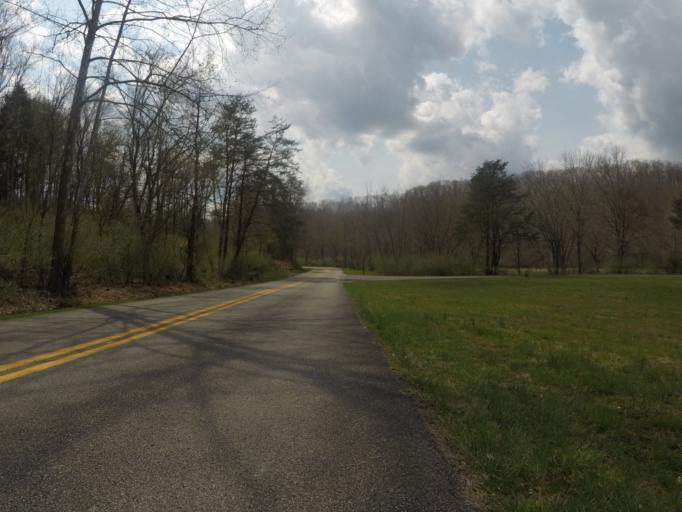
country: US
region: West Virginia
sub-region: Wayne County
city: Lavalette
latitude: 38.3102
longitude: -82.3578
